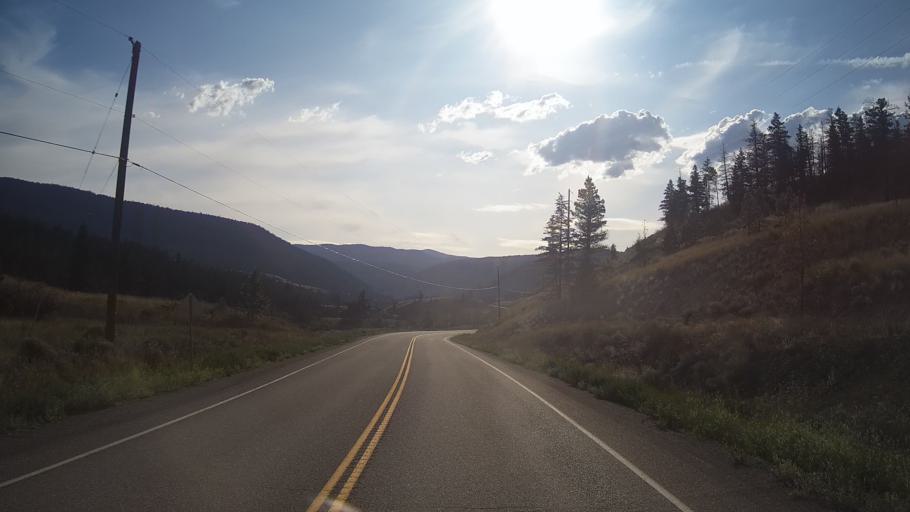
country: CA
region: British Columbia
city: Cache Creek
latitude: 50.8870
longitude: -121.4414
